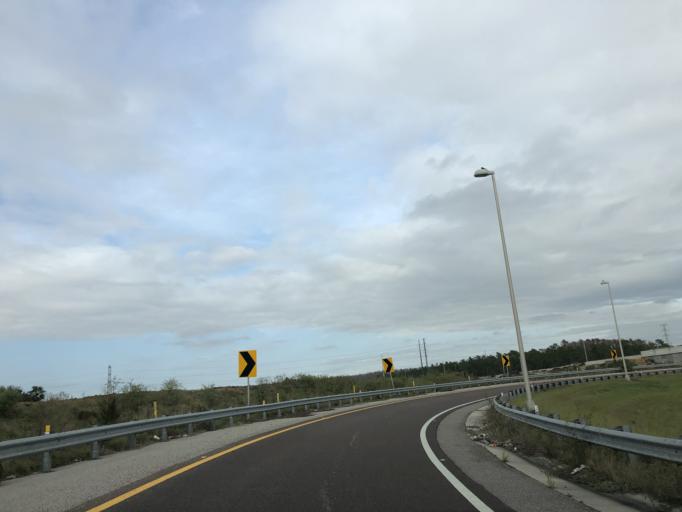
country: US
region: Florida
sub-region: Orange County
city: Southchase
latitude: 28.3693
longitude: -81.3917
